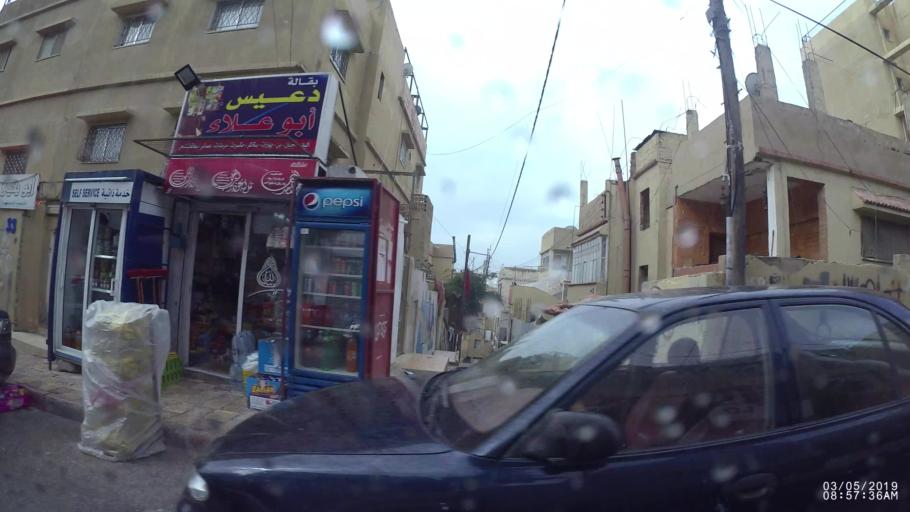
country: JO
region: Amman
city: Amman
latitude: 31.9586
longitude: 35.9383
